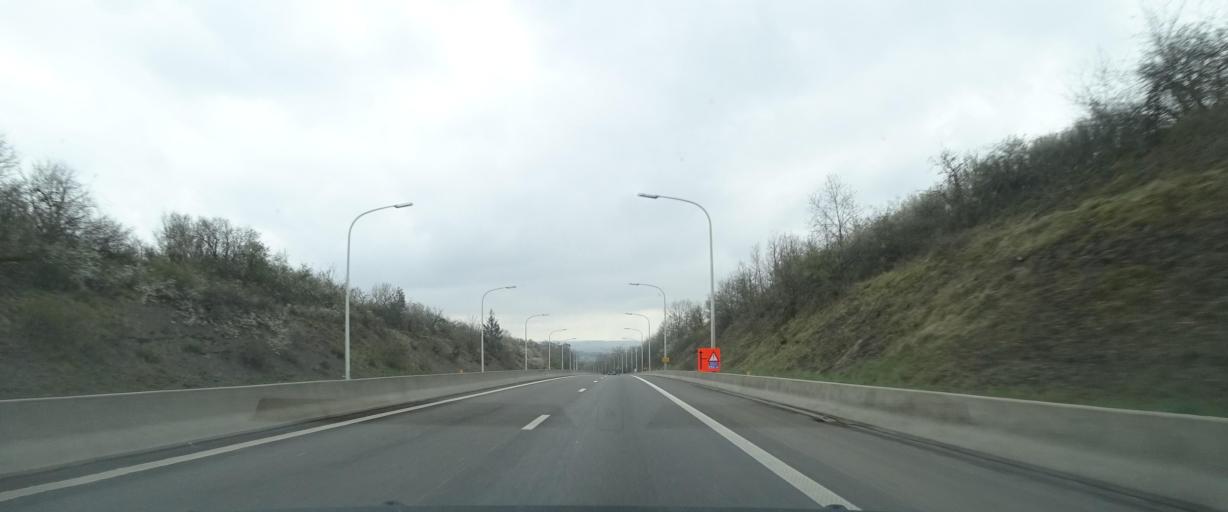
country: BE
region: Wallonia
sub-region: Province du Luxembourg
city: Marche-en-Famenne
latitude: 50.2582
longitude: 5.2650
